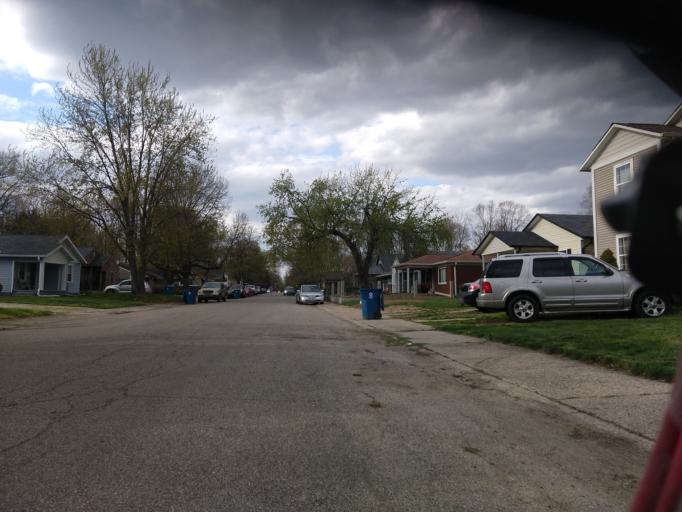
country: US
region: Indiana
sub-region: Marion County
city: Broad Ripple
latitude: 39.8369
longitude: -86.1289
